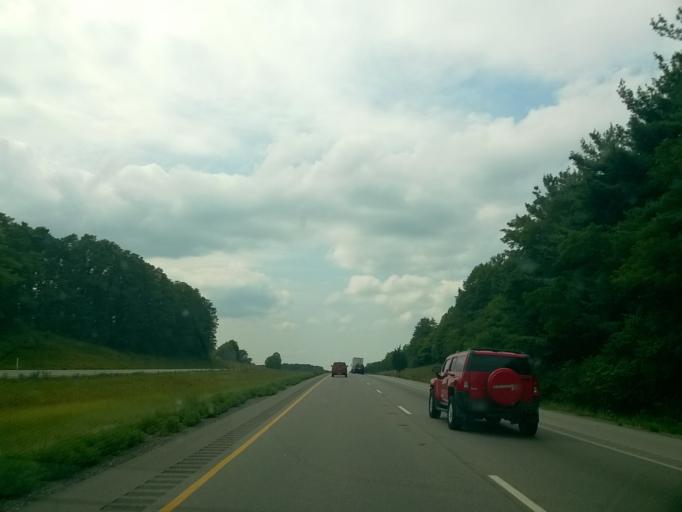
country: US
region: Indiana
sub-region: Putnam County
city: Cloverdale
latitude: 39.5331
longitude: -86.8308
